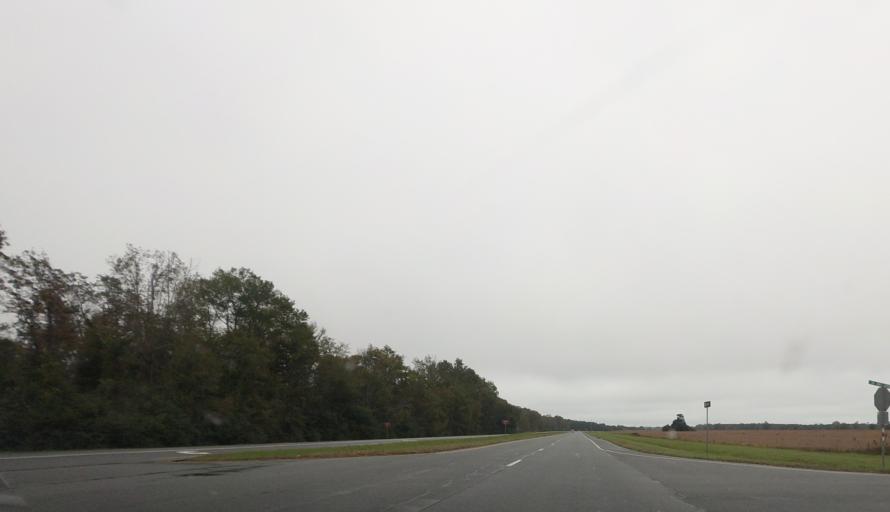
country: US
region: Georgia
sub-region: Taylor County
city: Reynolds
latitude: 32.5581
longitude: -84.0711
